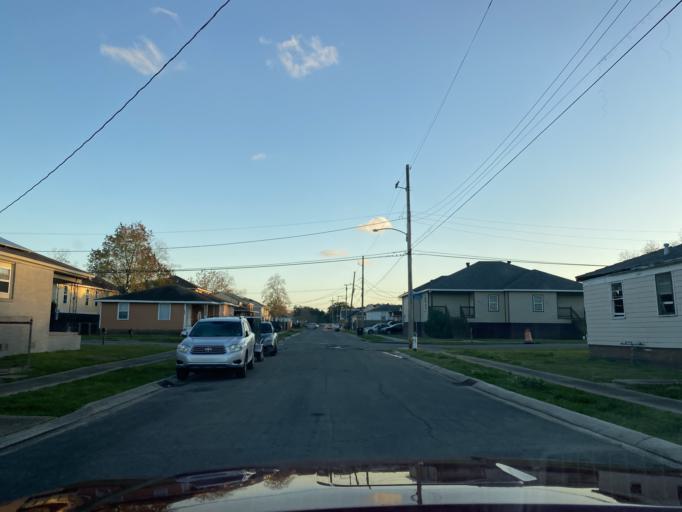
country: US
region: Louisiana
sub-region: Orleans Parish
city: New Orleans
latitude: 30.0206
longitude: -90.0540
